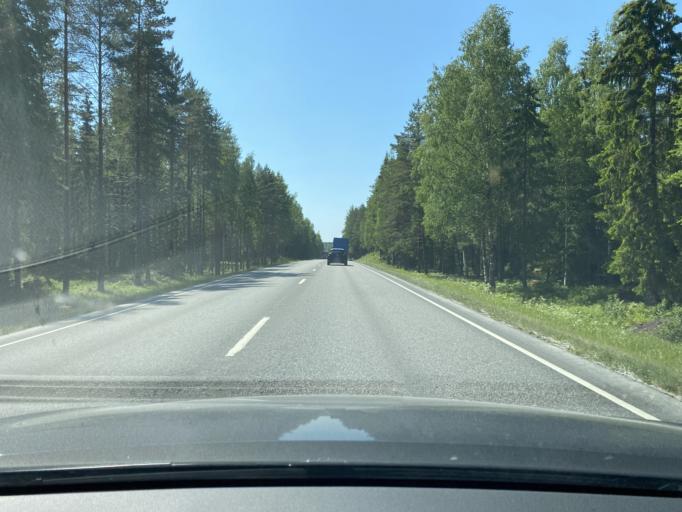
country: FI
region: Pirkanmaa
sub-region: Lounais-Pirkanmaa
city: Mouhijaervi
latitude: 61.3865
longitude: 23.1987
